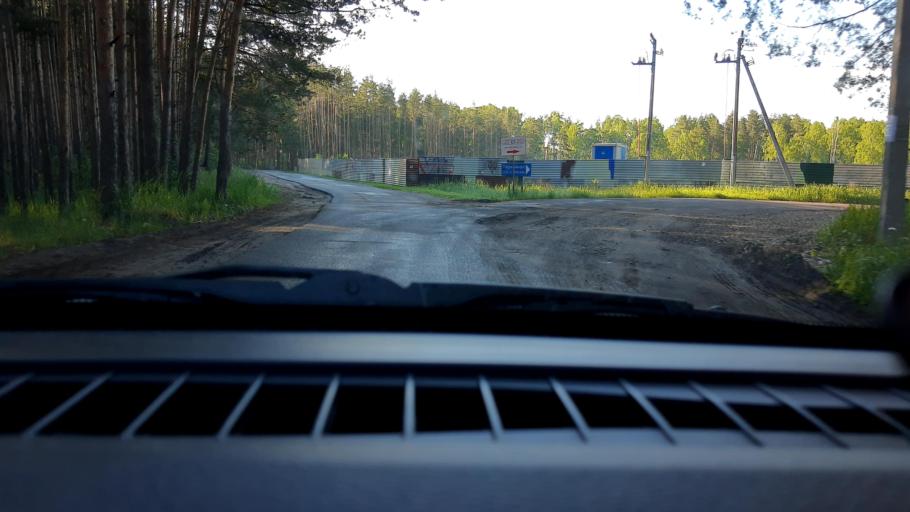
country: RU
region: Nizjnij Novgorod
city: Gorbatovka
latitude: 56.3055
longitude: 43.7404
